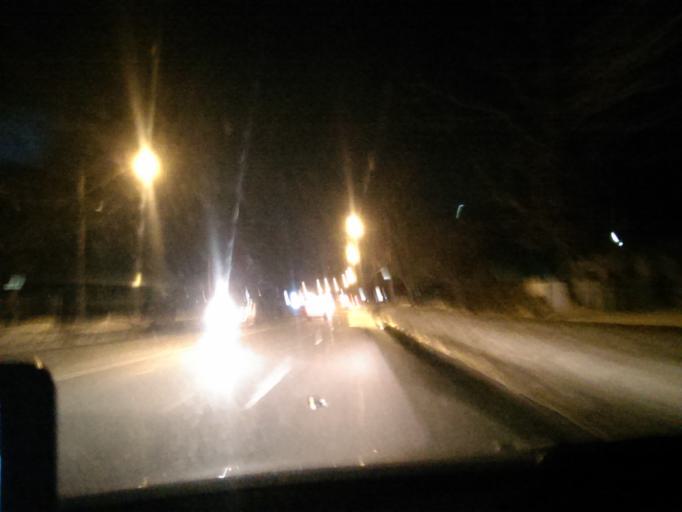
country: US
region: Massachusetts
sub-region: Hampden County
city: Ludlow
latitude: 42.1209
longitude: -72.4981
